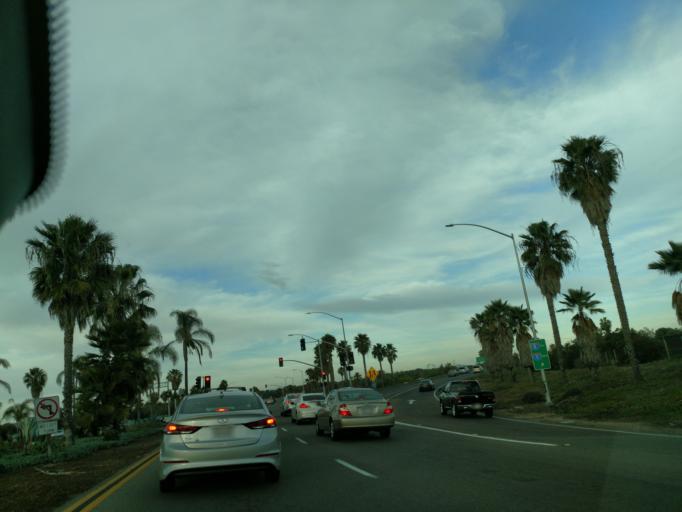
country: US
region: California
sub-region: San Diego County
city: Coronado
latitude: 32.7540
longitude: -117.2365
